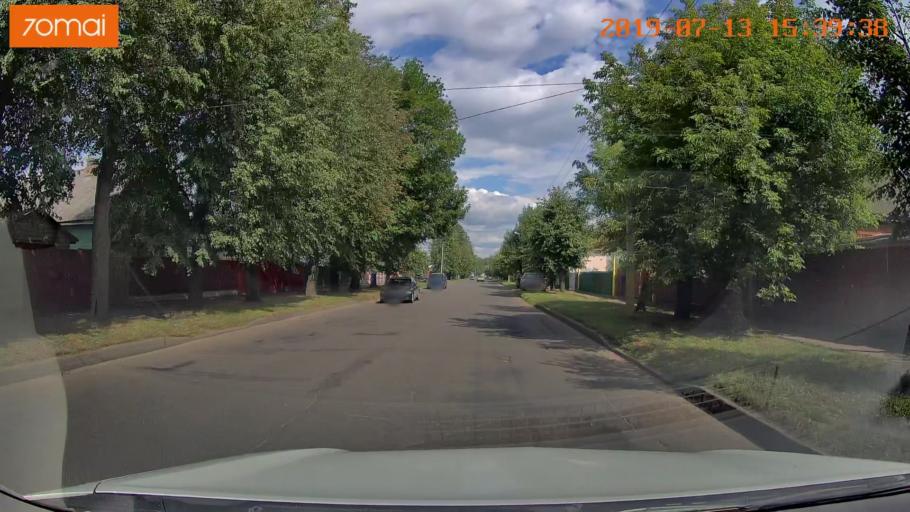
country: BY
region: Mogilev
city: Babruysk
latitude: 53.1351
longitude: 29.1834
